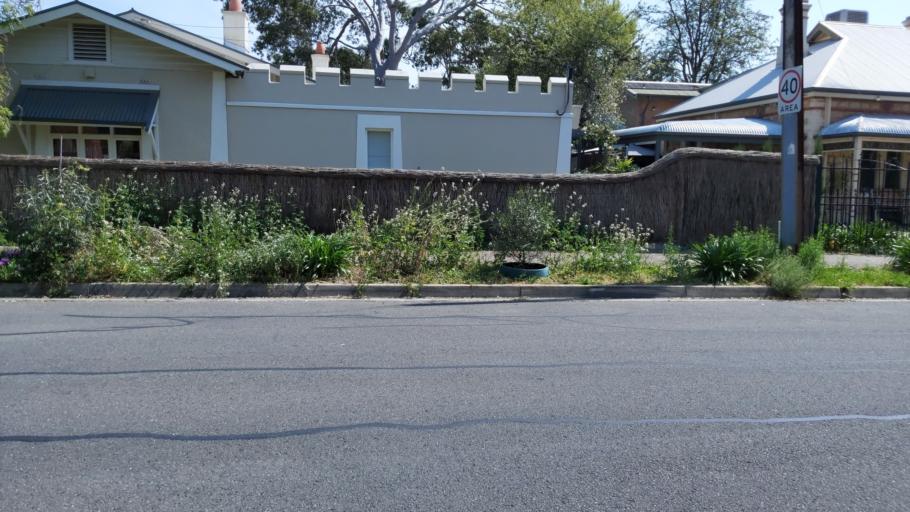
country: AU
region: South Australia
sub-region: Unley
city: Fullarton
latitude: -34.9522
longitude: 138.6289
